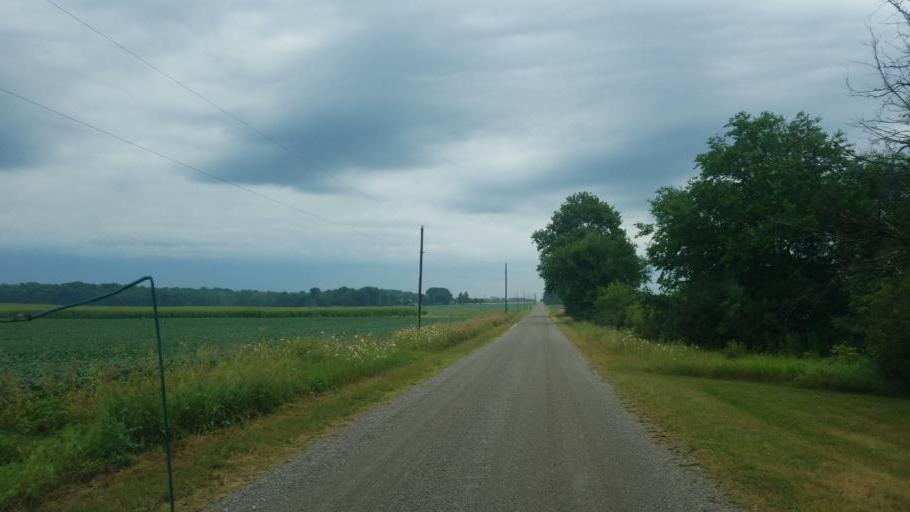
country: US
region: Indiana
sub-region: DeKalb County
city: Butler
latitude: 41.4428
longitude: -84.9042
